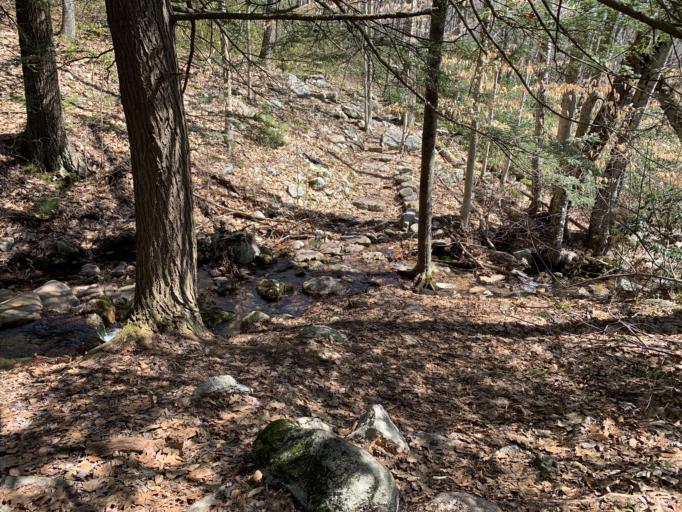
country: US
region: Pennsylvania
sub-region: Luzerne County
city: White Haven
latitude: 41.1726
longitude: -75.7119
